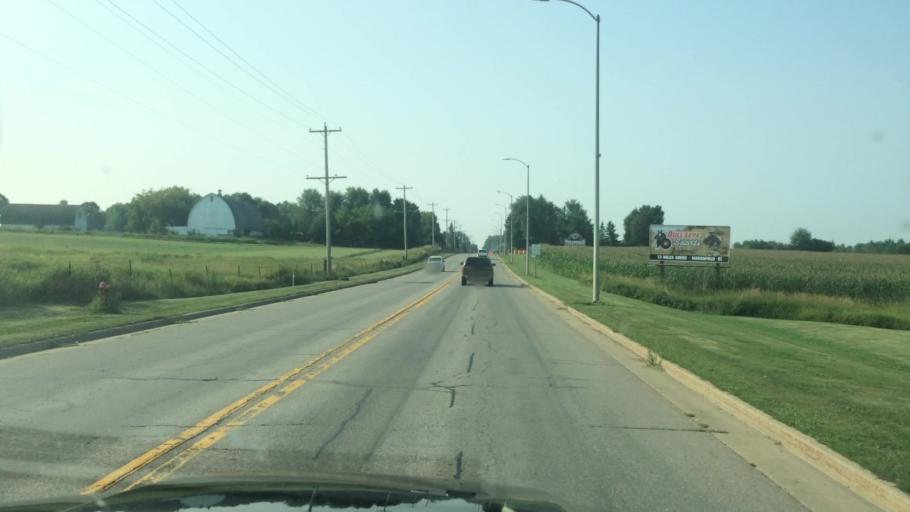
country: US
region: Wisconsin
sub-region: Marathon County
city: Stratford
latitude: 44.8147
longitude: -90.0792
